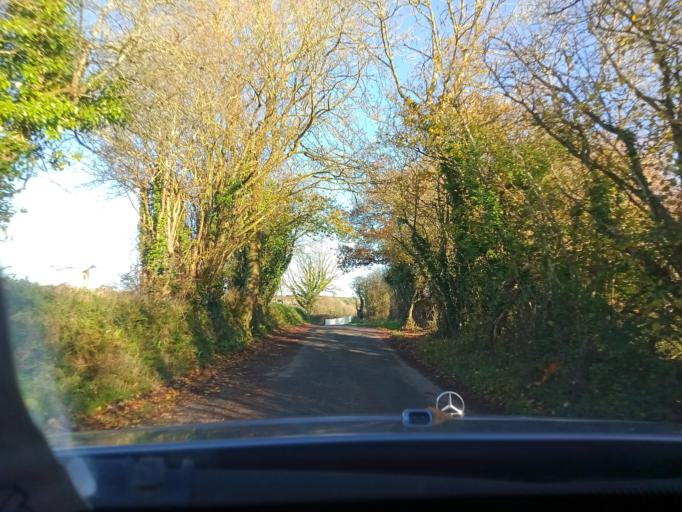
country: IE
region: Leinster
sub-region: Kilkenny
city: Mooncoin
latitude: 52.3363
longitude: -7.2574
